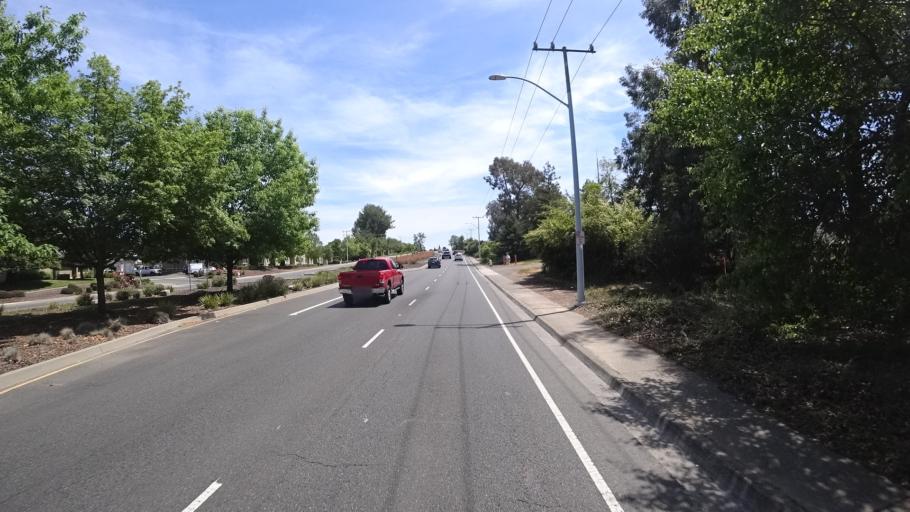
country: US
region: California
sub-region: Placer County
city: Rocklin
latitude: 38.7838
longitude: -121.2465
